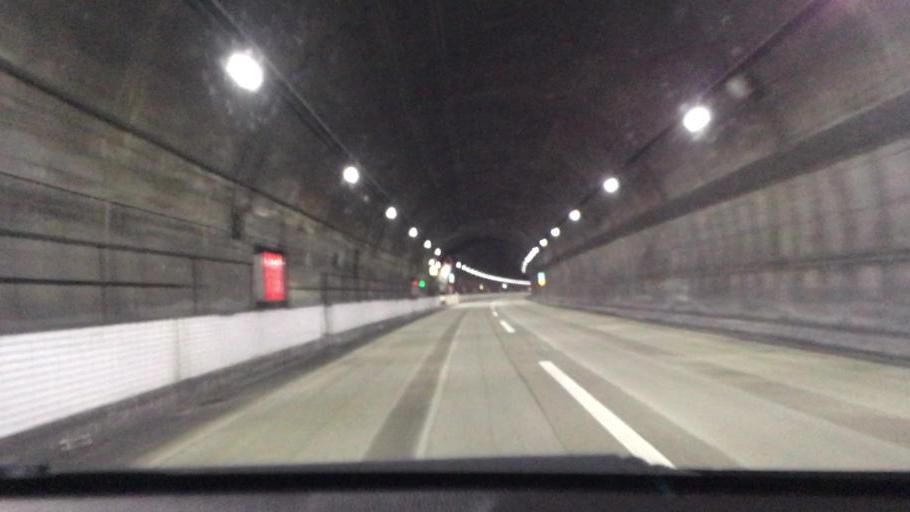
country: JP
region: Yamaguchi
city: Hofu
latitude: 34.0552
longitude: 131.6271
